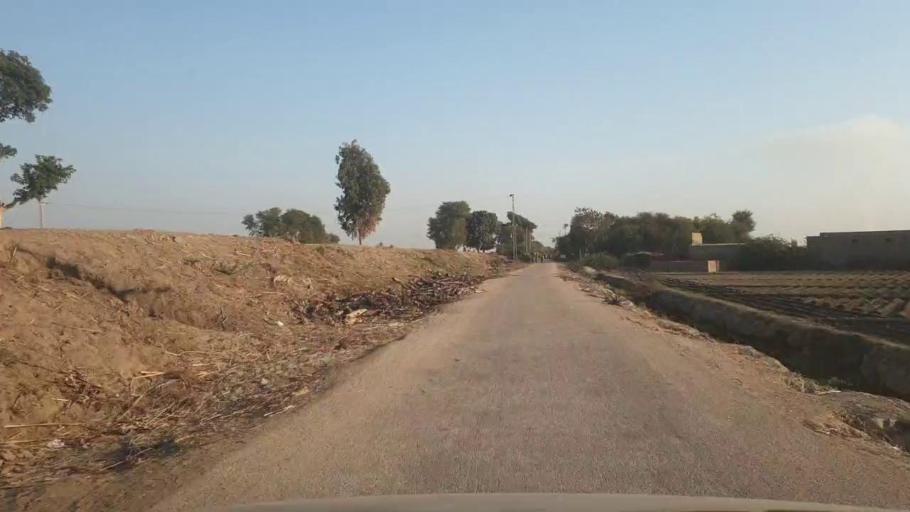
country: PK
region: Sindh
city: Chambar
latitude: 25.2894
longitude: 68.8958
